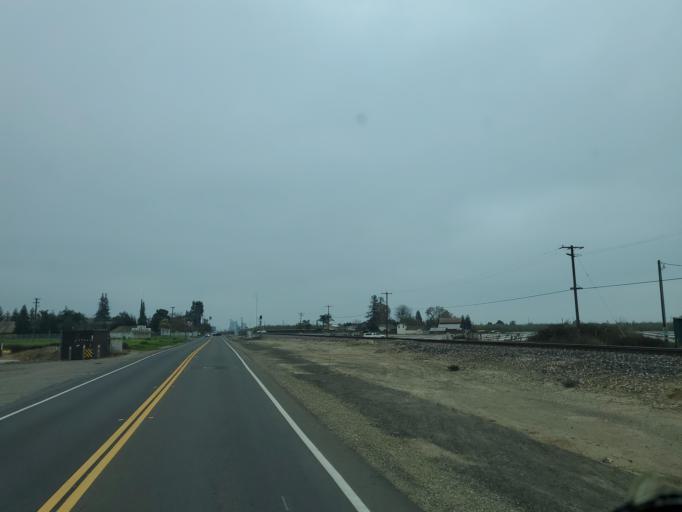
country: US
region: California
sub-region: Stanislaus County
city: Hughson
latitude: 37.5902
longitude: -120.8623
